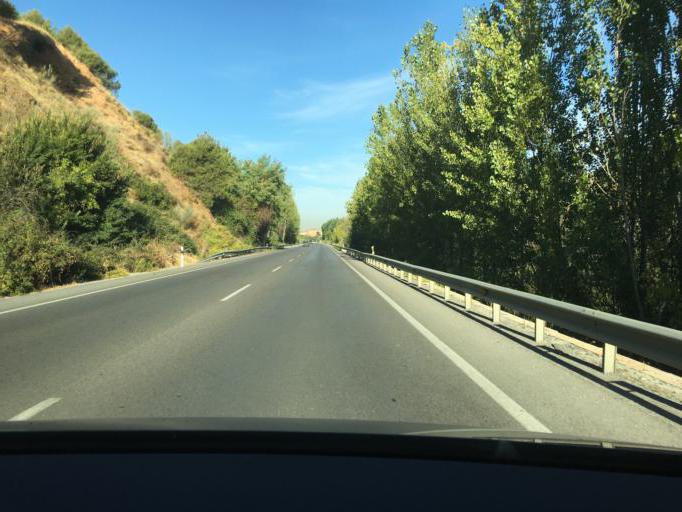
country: ES
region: Andalusia
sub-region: Provincia de Granada
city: Cenes de la Vega
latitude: 37.1587
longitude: -3.5536
